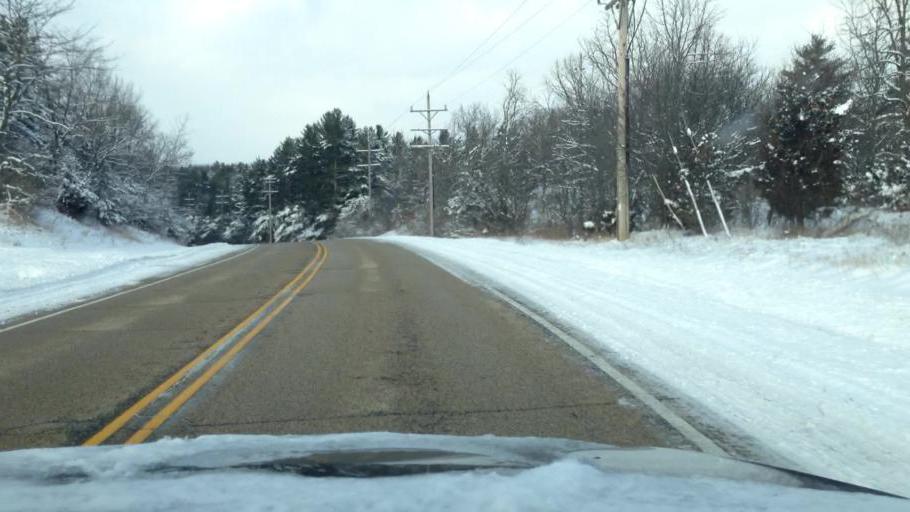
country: US
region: Wisconsin
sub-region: Walworth County
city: East Troy
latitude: 42.8318
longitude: -88.4238
